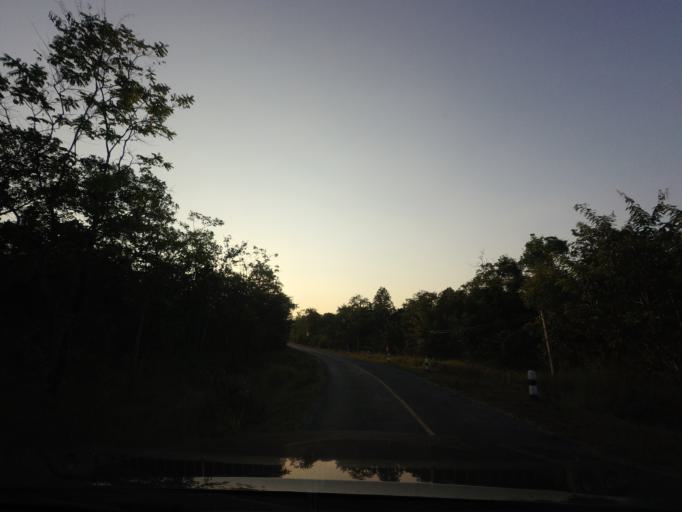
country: TH
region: Nan
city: Na Noi
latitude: 18.3052
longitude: 100.7464
